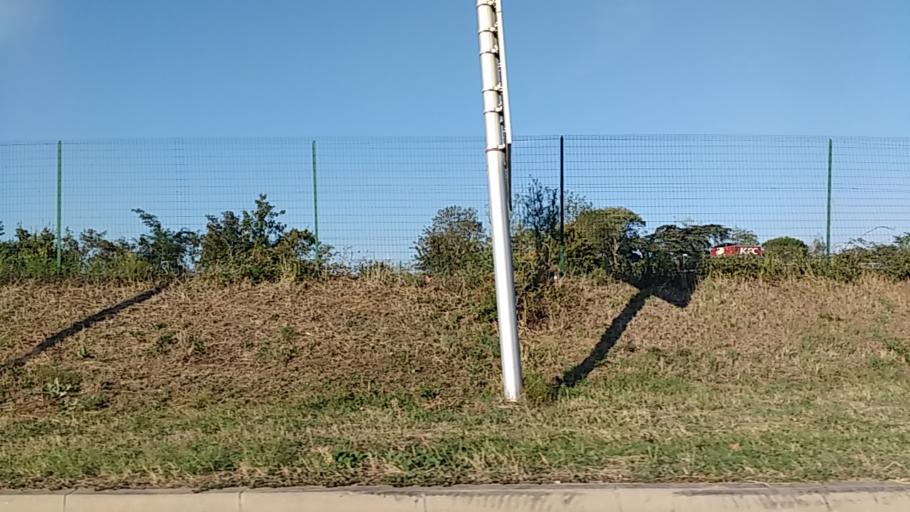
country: FR
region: Midi-Pyrenees
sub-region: Departement de la Haute-Garonne
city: Cugnaux
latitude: 43.5684
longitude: 1.3761
